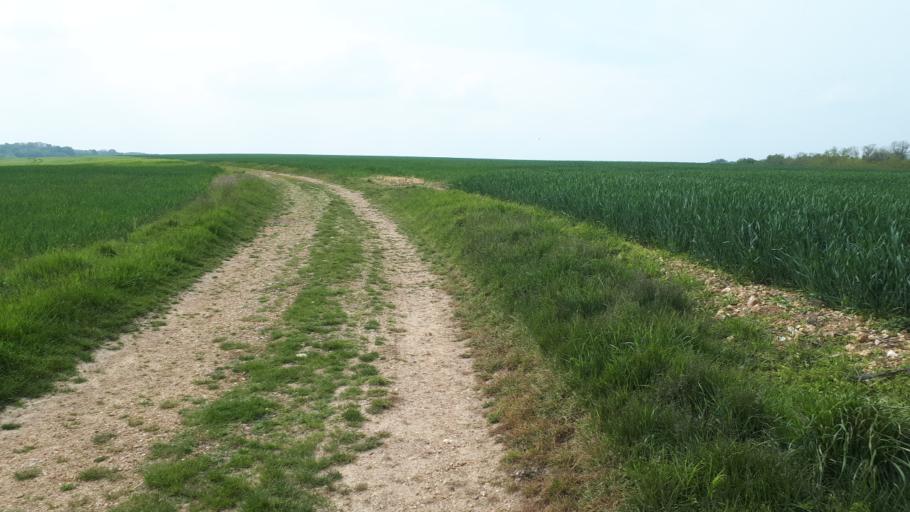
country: FR
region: Centre
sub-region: Departement du Loir-et-Cher
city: Lunay
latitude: 47.8245
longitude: 0.9393
